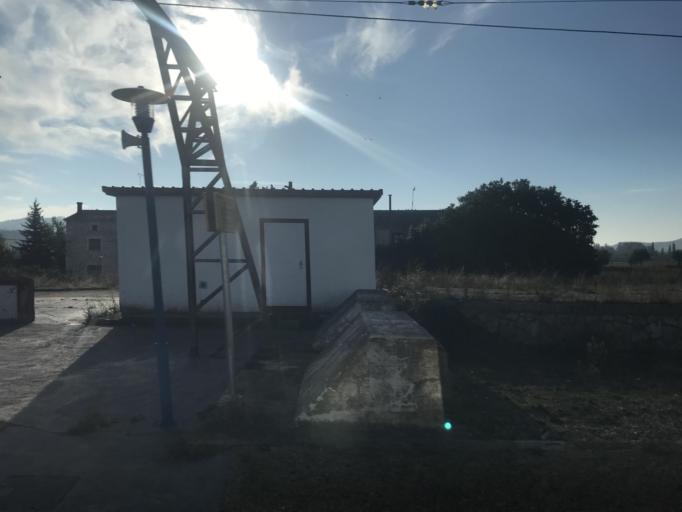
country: ES
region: Castille and Leon
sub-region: Provincia de Burgos
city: Villaquiran de los Infantes
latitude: 42.2157
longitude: -4.0011
